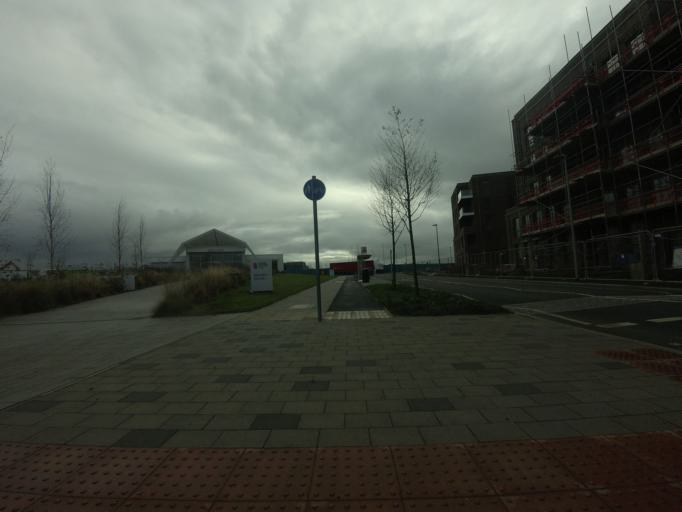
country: GB
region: England
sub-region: Greater London
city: Becontree
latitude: 51.5251
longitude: 0.1242
